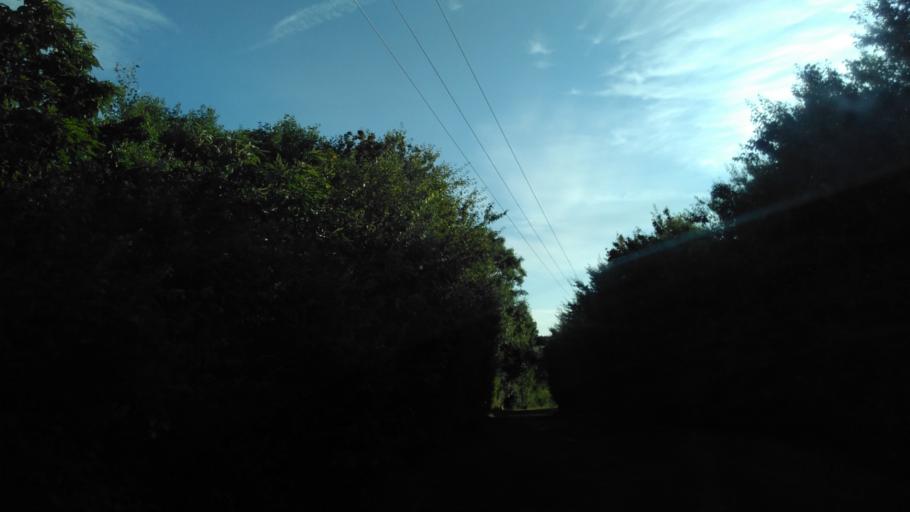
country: GB
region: England
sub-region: Kent
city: Dunkirk
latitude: 51.3038
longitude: 0.9874
